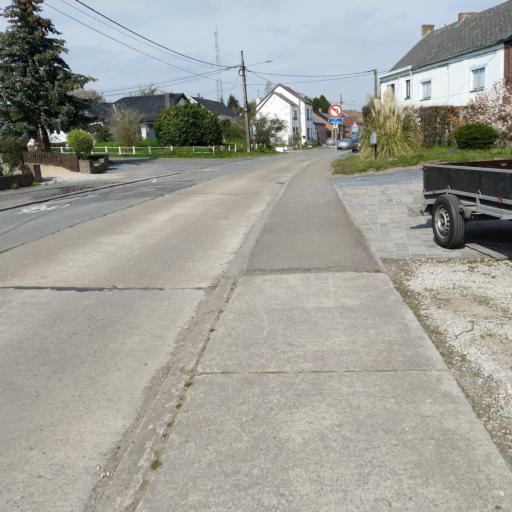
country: BE
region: Wallonia
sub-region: Province du Hainaut
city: Chasse Royale
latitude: 50.4316
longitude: 3.9590
